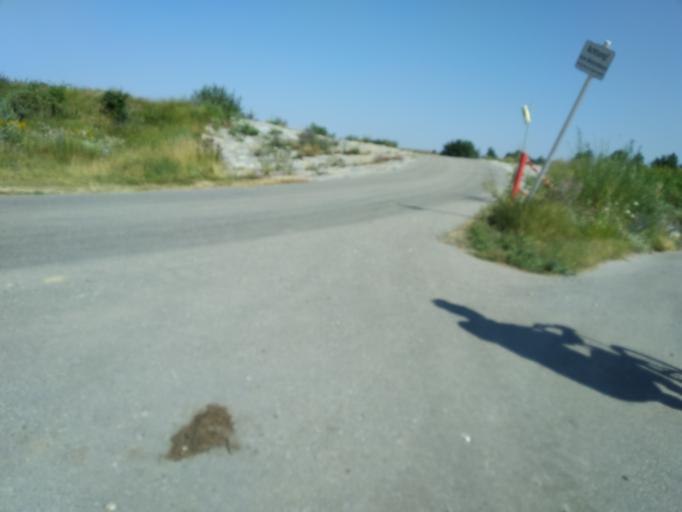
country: AT
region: Lower Austria
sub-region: Politischer Bezirk Mistelbach
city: Wolkersdorf im Weinviertel
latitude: 48.3833
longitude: 16.4970
